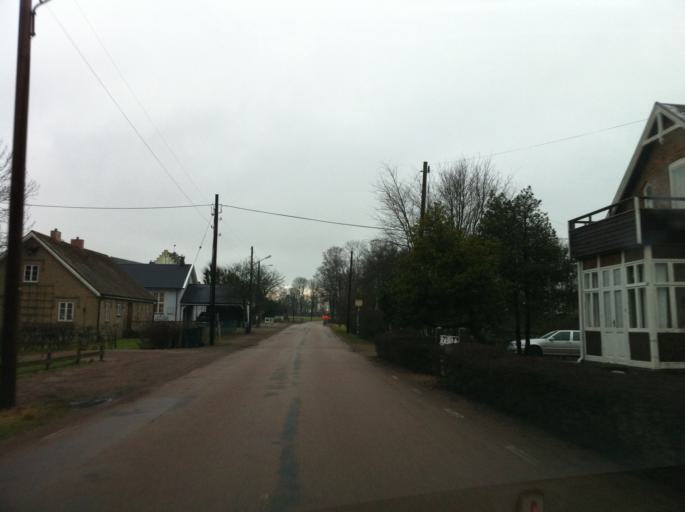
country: SE
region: Skane
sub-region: Helsingborg
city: Barslov
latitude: 55.9854
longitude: 12.8500
